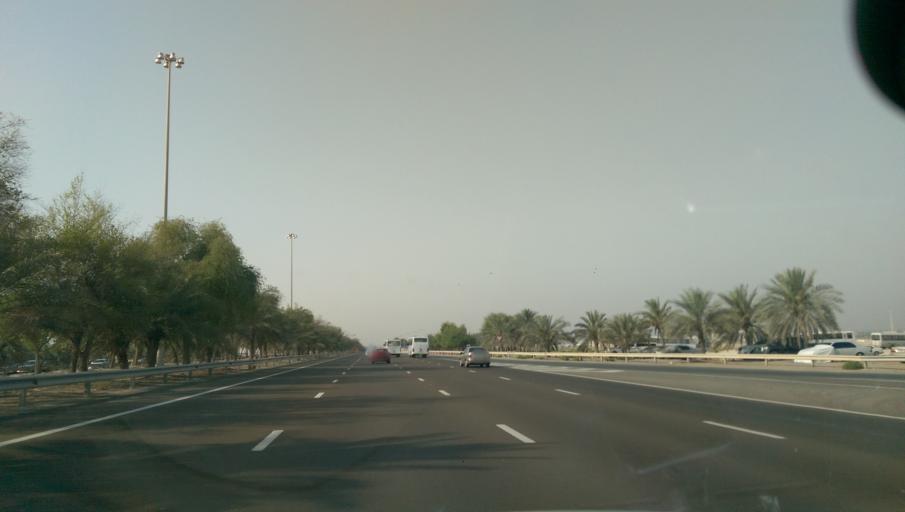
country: AE
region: Abu Dhabi
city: Abu Dhabi
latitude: 24.4424
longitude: 54.6783
